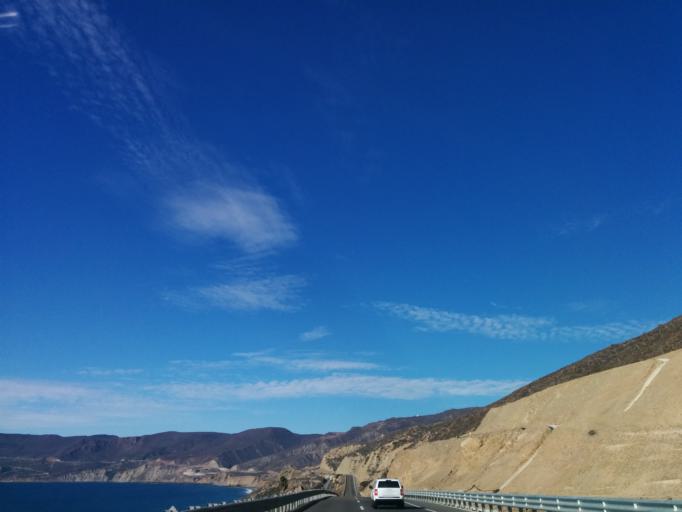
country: MX
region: Baja California
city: El Sauzal
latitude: 31.9427
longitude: -116.7541
